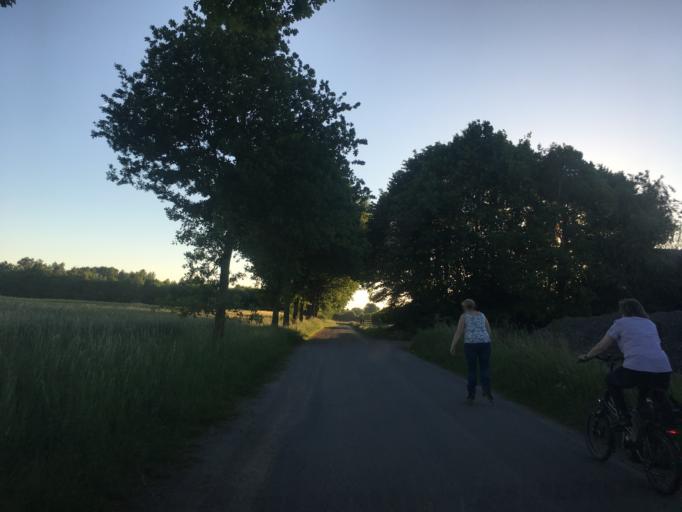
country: DE
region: North Rhine-Westphalia
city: Ludinghausen
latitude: 51.7440
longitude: 7.4685
